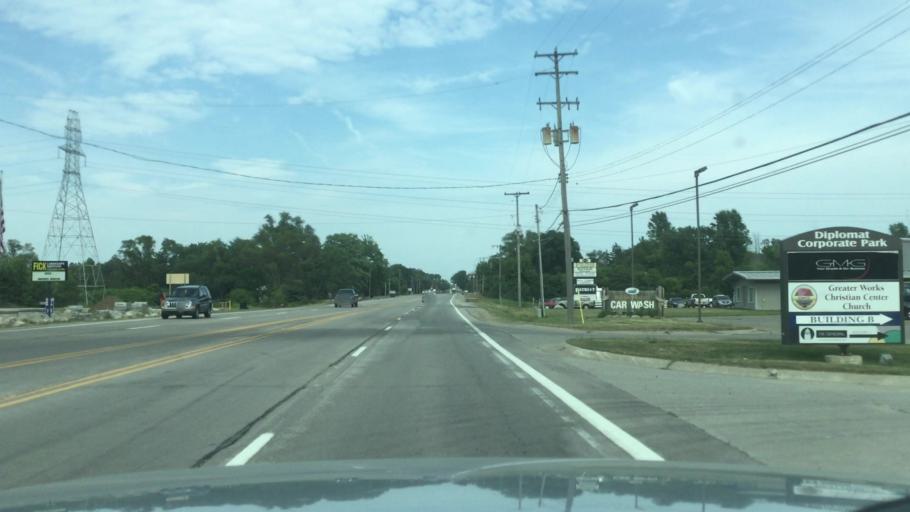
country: US
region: Michigan
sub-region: Genesee County
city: Swartz Creek
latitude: 43.0013
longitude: -83.8101
